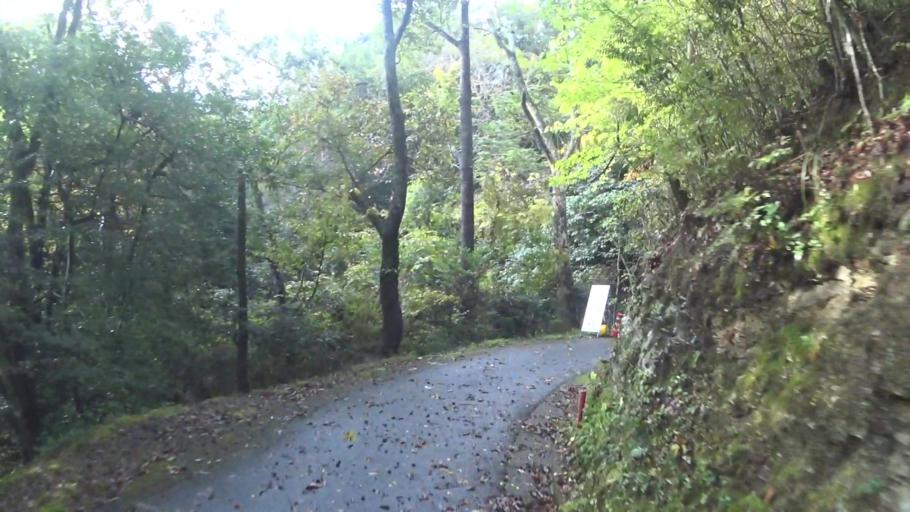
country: JP
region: Kyoto
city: Ayabe
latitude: 35.2742
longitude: 135.2305
